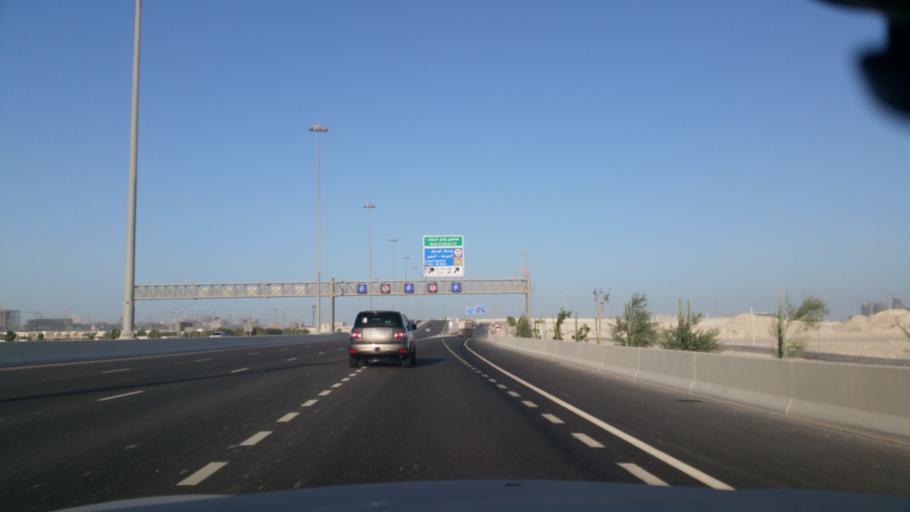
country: QA
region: Baladiyat Umm Salal
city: Umm Salal Muhammad
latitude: 25.4005
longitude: 51.4832
